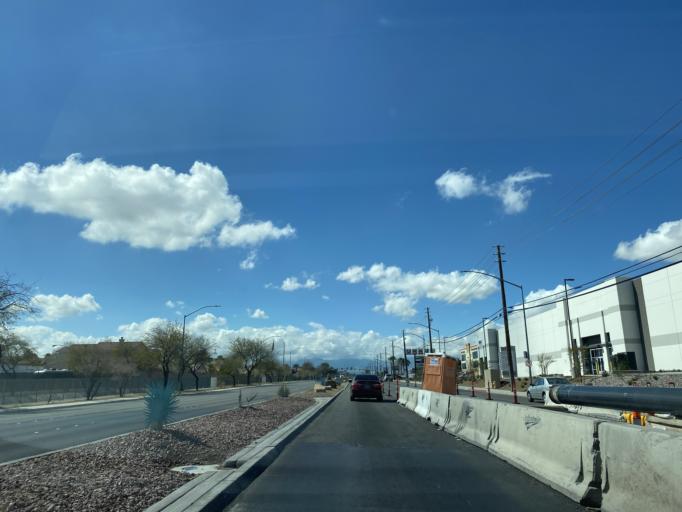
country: US
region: Nevada
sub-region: Clark County
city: North Las Vegas
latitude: 36.2396
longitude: -115.1392
